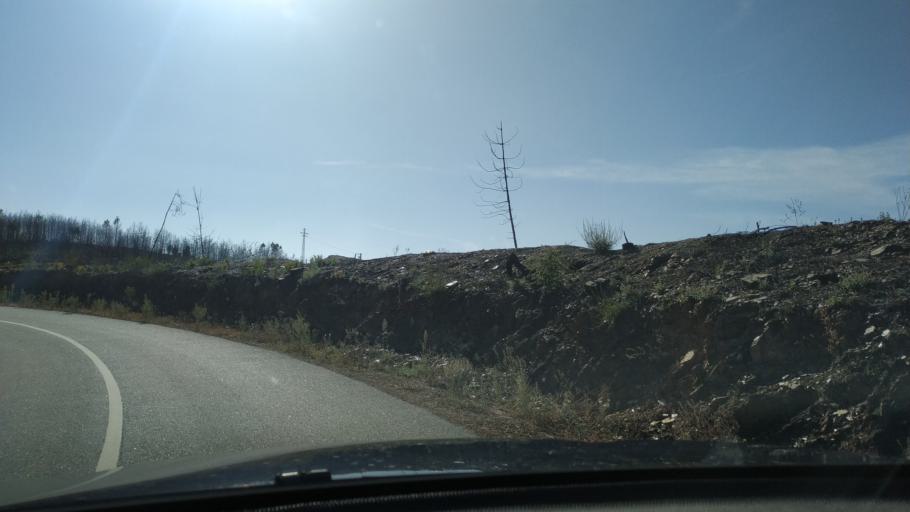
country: PT
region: Vila Real
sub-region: Sabrosa
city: Vilela
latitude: 41.2358
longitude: -7.6406
